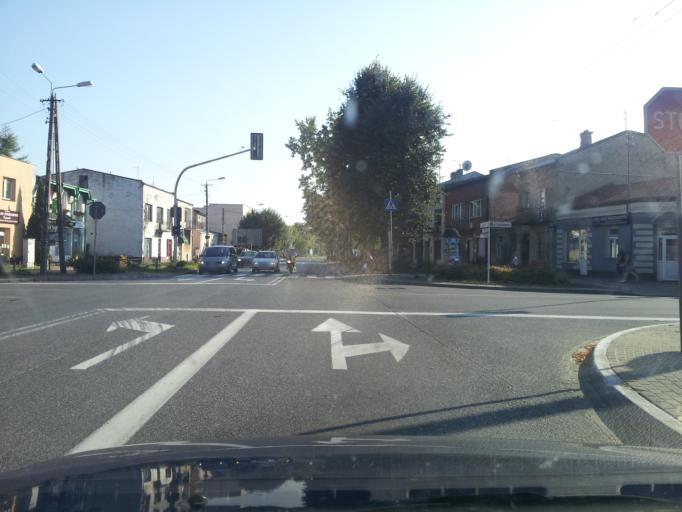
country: PL
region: Masovian Voivodeship
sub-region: Powiat warszawski zachodni
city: Leszno
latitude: 52.2580
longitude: 20.5912
